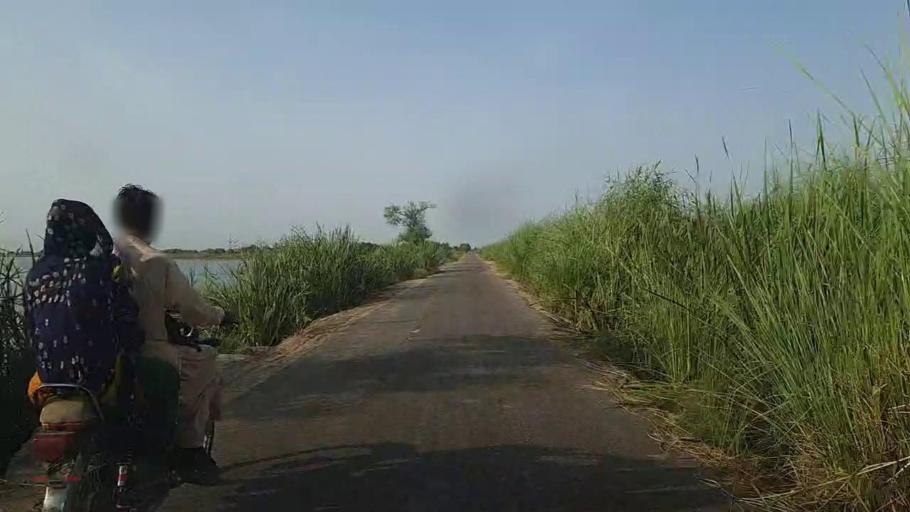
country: PK
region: Sindh
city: Khairpur
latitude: 28.0804
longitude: 69.8140
